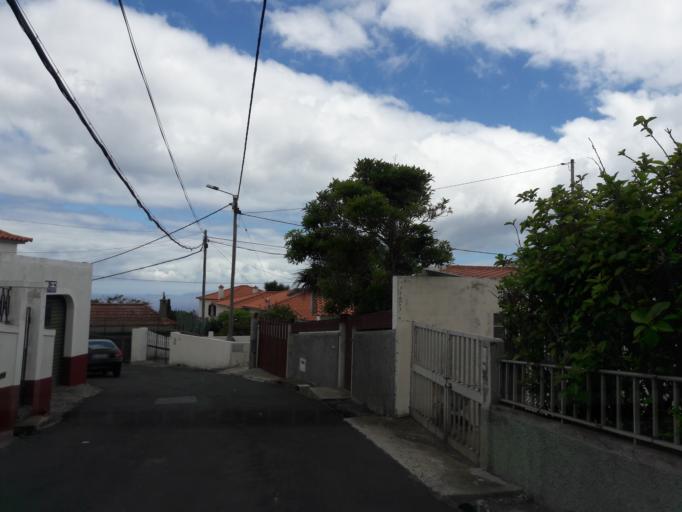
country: PT
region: Madeira
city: Canico
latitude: 32.6482
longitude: -16.8486
